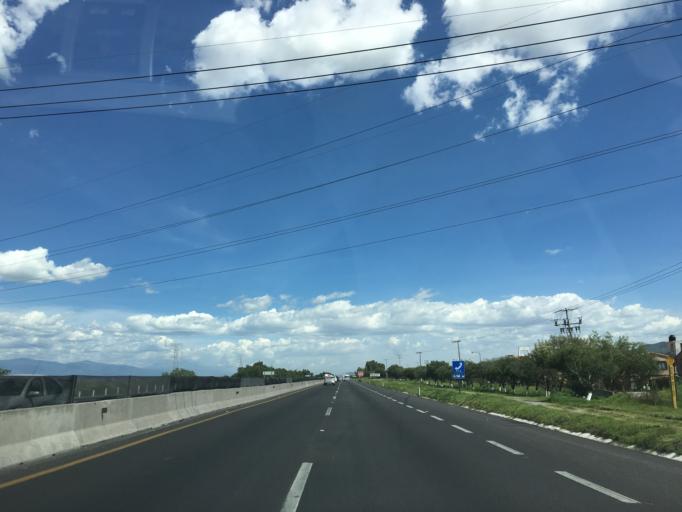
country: MX
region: Mexico
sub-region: Jaltenco
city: Alborada Jaltenco
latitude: 19.6706
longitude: -99.0688
